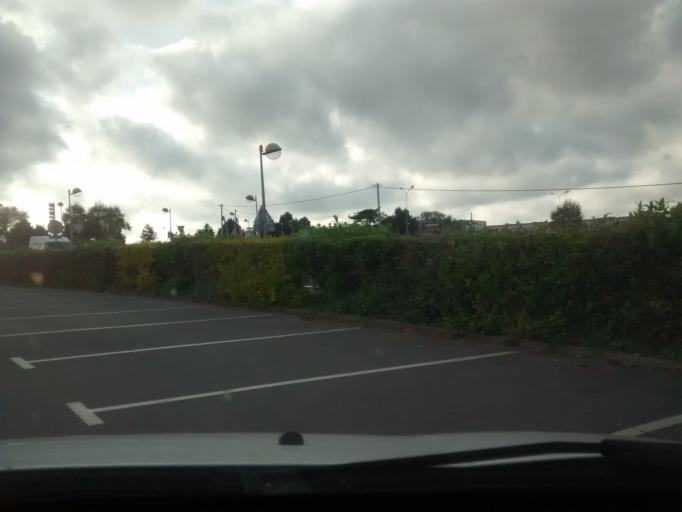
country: FR
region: Brittany
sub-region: Departement des Cotes-d'Armor
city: Lannion
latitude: 48.7527
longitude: -3.4568
